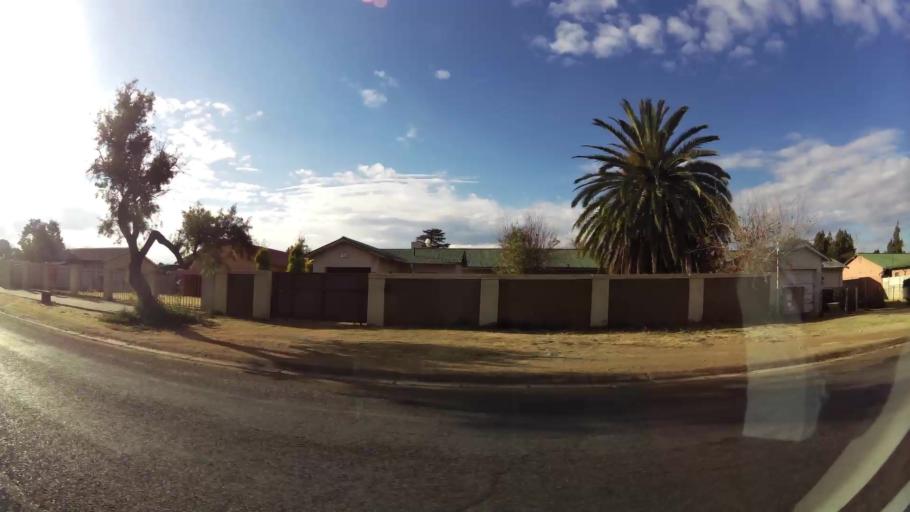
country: ZA
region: Orange Free State
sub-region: Lejweleputswa District Municipality
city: Welkom
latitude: -27.9883
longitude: 26.7424
